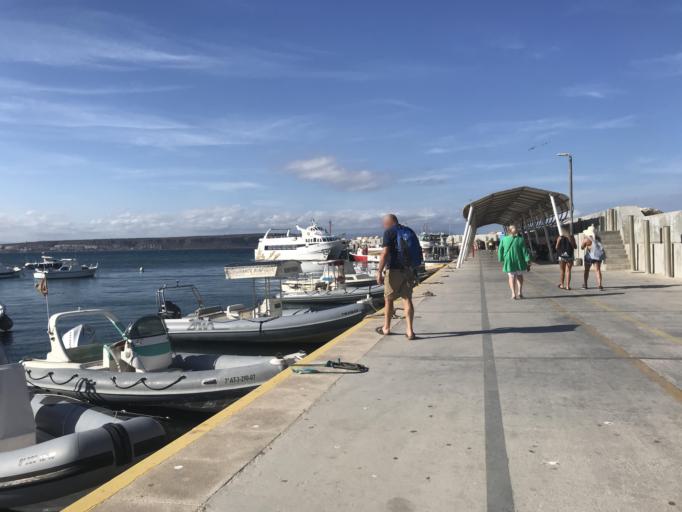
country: ES
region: Valencia
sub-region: Provincia de Alicante
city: Santa Pola
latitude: 38.1666
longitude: -0.4779
